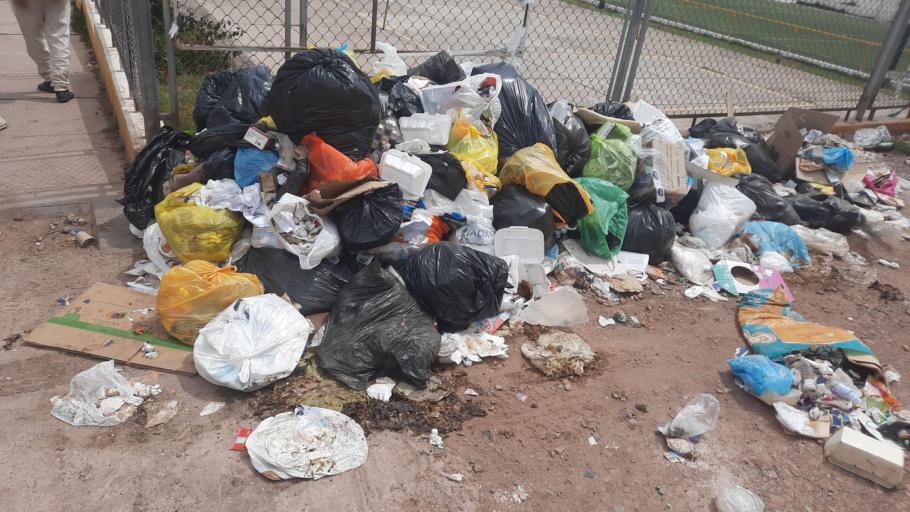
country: PE
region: Cusco
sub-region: Provincia de Cusco
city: Saylla
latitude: -13.5344
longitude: -71.9019
